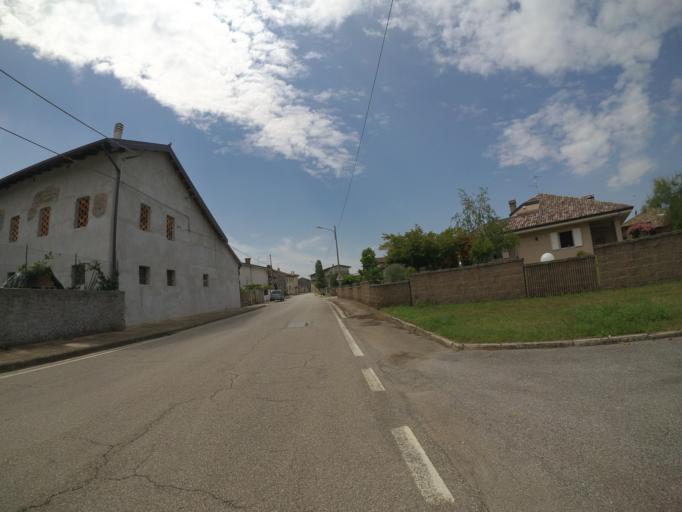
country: IT
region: Friuli Venezia Giulia
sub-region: Provincia di Udine
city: Bertiolo
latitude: 45.9392
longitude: 13.0722
